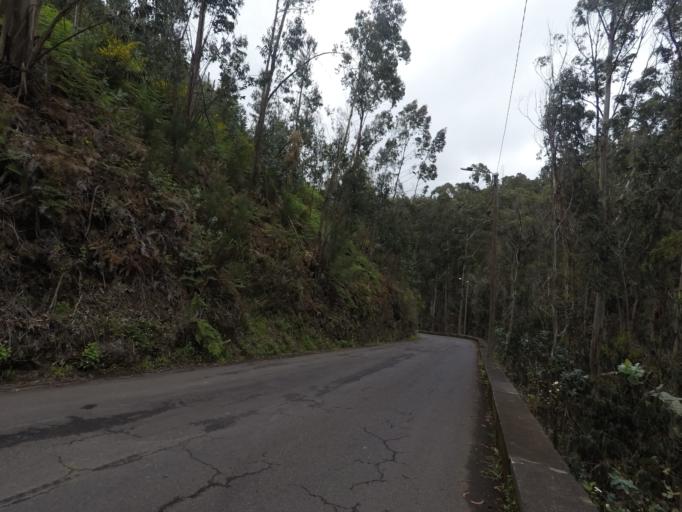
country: PT
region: Madeira
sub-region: Calheta
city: Estreito da Calheta
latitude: 32.7547
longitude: -17.1962
